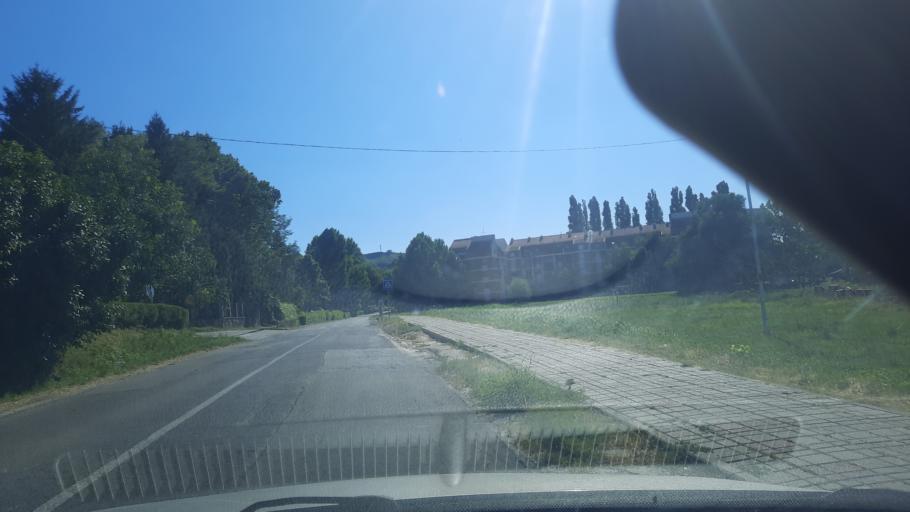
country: RS
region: Autonomna Pokrajina Vojvodina
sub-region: Juznobacki Okrug
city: Beocin
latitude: 45.2083
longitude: 19.7268
